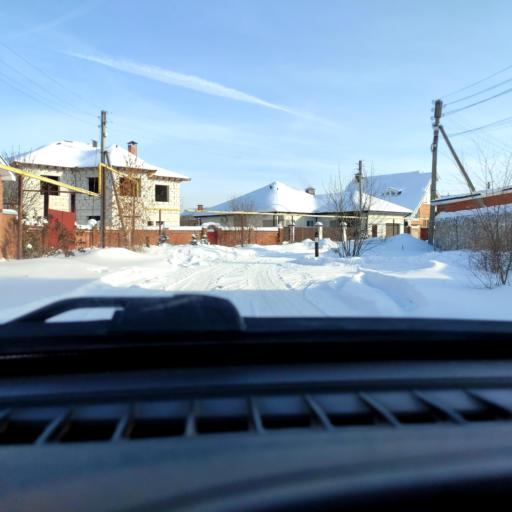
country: RU
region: Samara
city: Podstepki
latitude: 53.5118
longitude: 49.1862
